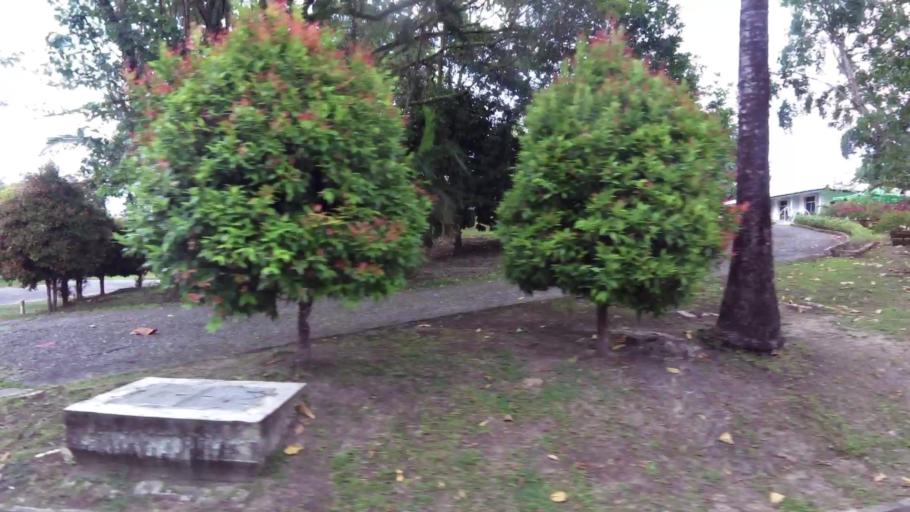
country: BN
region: Brunei and Muara
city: Bandar Seri Begawan
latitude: 4.9489
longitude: 114.9604
